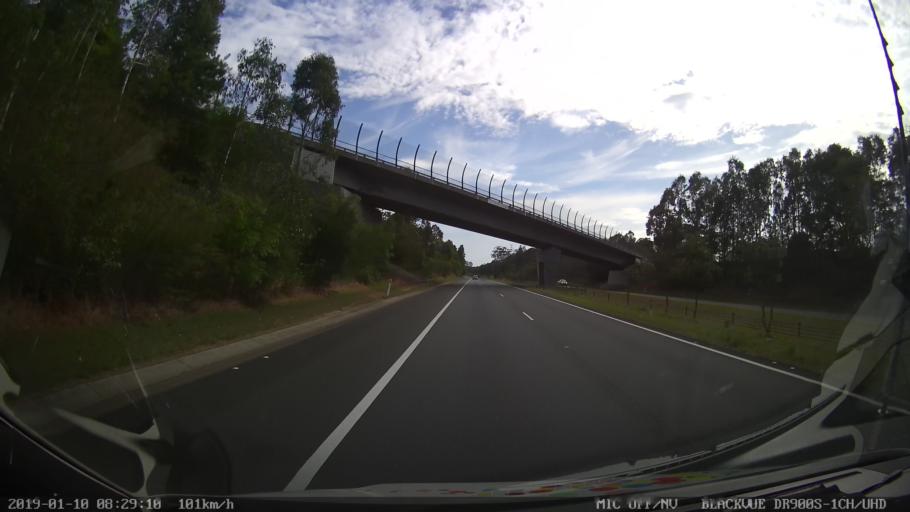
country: AU
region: New South Wales
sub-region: Coffs Harbour
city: Bonville
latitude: -30.3858
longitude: 153.0422
